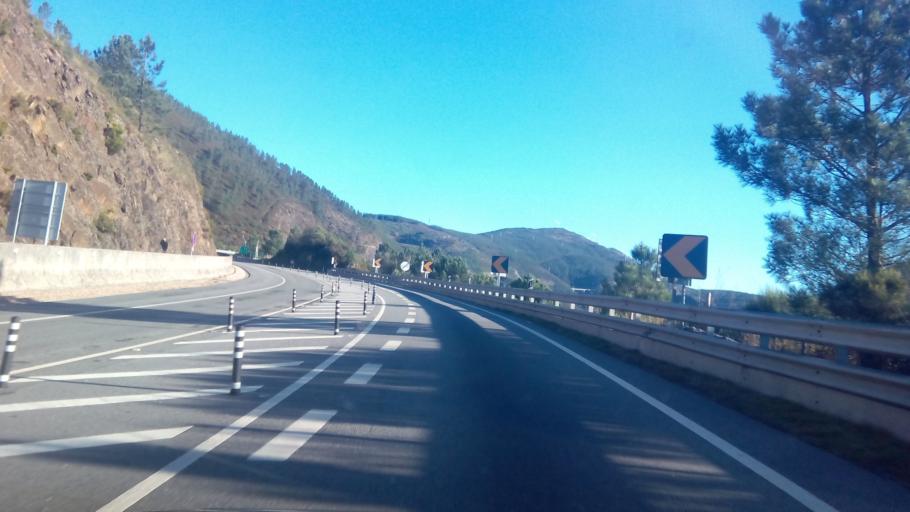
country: PT
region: Porto
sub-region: Baiao
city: Valadares
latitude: 41.2615
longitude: -7.9476
